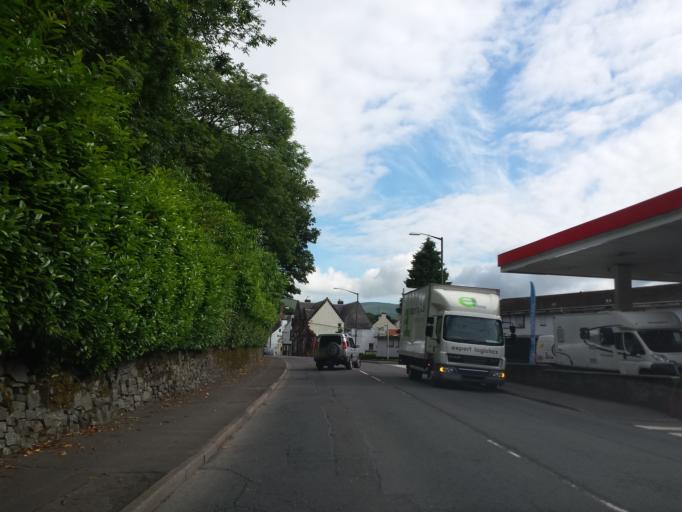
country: GB
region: Scotland
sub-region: Dumfries and Galloway
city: Moffat
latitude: 55.3307
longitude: -3.4444
